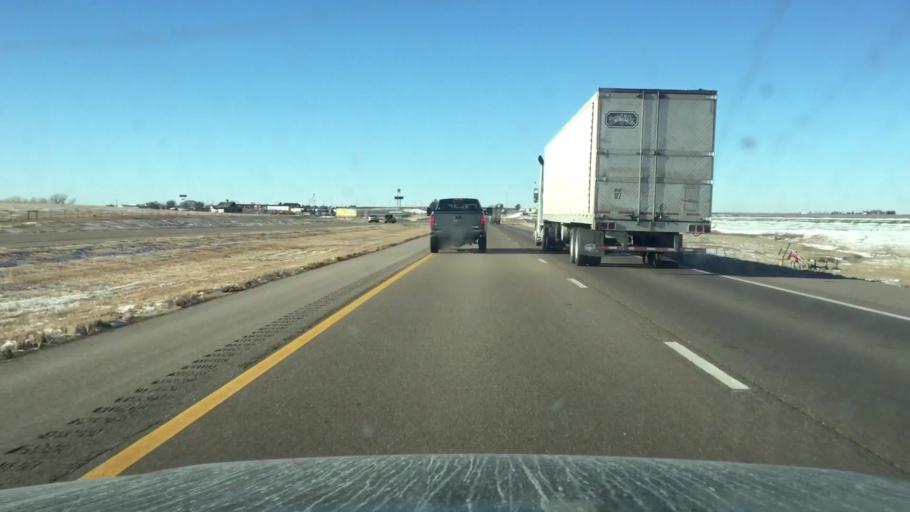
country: US
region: Kansas
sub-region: Logan County
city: Oakley
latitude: 39.1807
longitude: -100.8601
